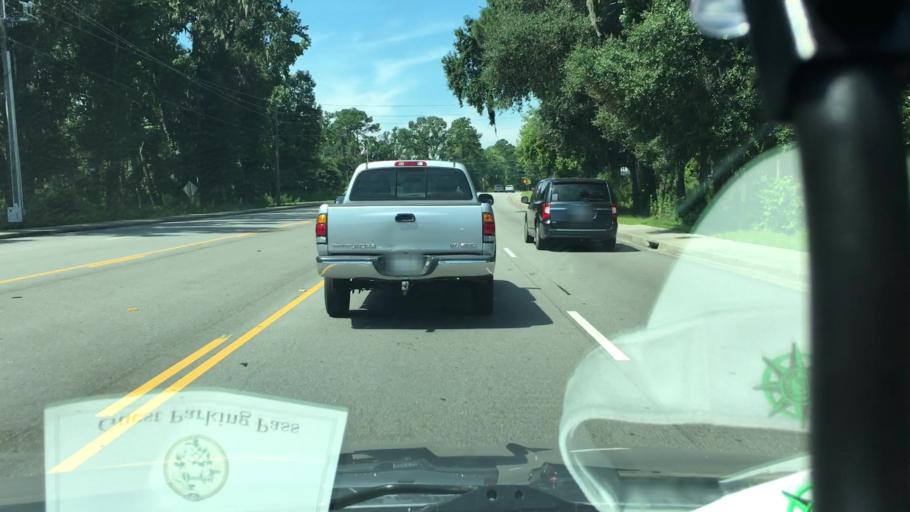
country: US
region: South Carolina
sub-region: Beaufort County
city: Burton
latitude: 32.4325
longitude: -80.7141
